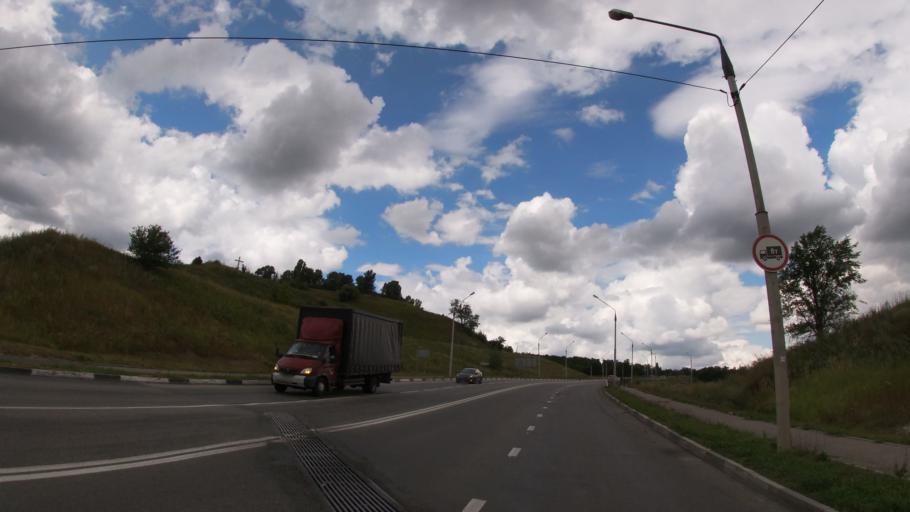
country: RU
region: Belgorod
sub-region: Belgorodskiy Rayon
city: Belgorod
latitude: 50.6178
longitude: 36.6164
